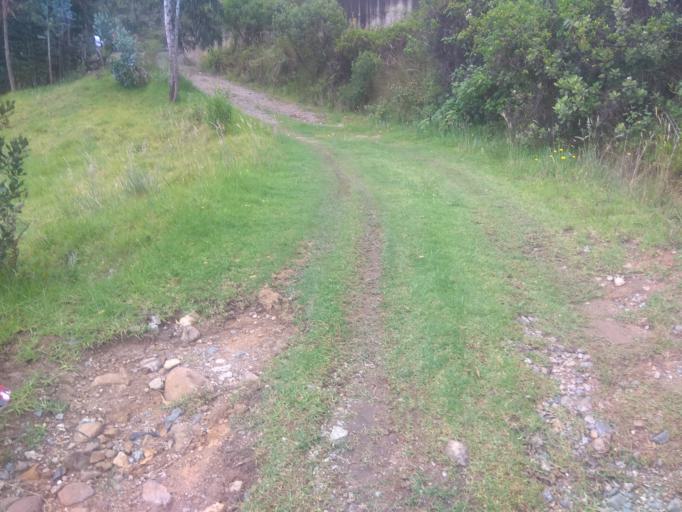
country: CO
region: Boyaca
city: Socota
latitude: 6.0094
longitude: -72.6718
